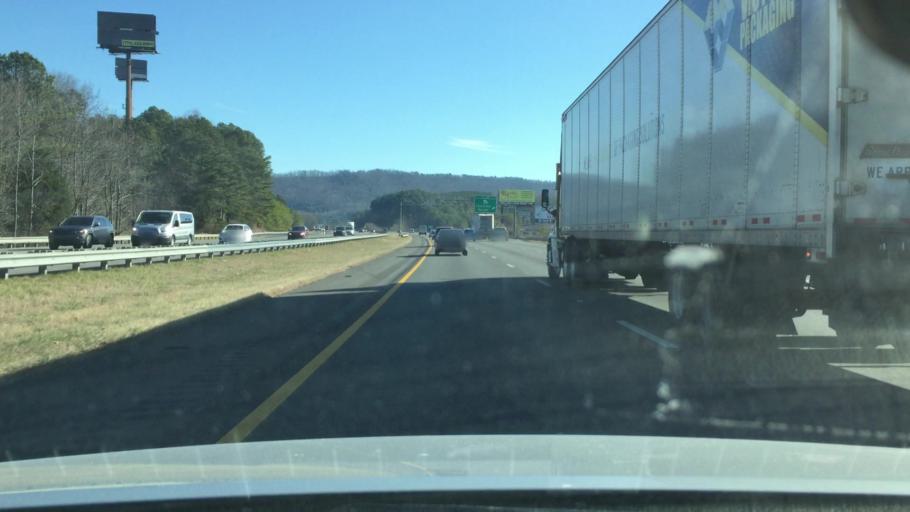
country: US
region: Georgia
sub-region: Whitfield County
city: Varnell
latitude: 34.8651
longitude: -85.0323
